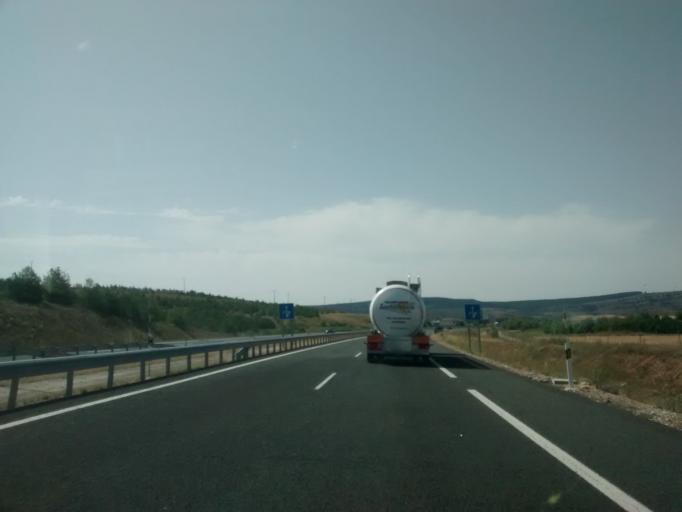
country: ES
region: Castille and Leon
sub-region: Provincia de Palencia
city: Aguilar de Campoo
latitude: 42.7920
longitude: -4.2368
